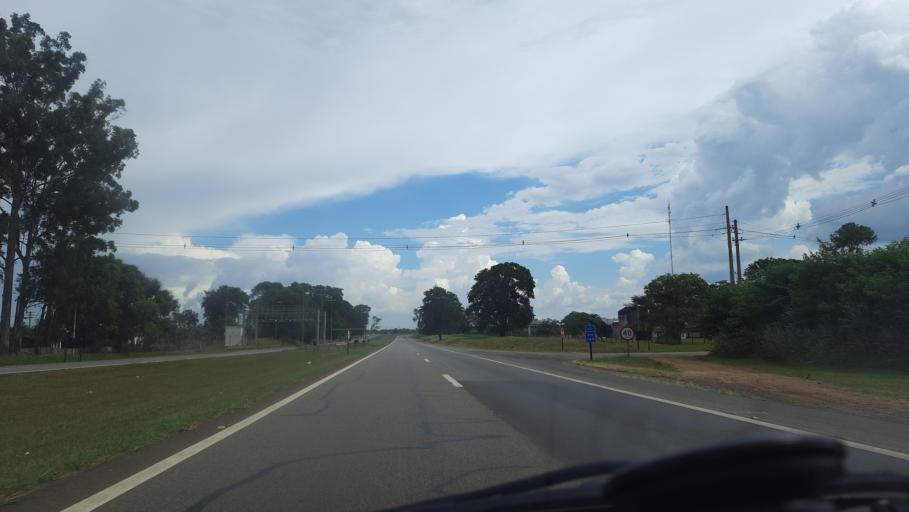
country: BR
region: Sao Paulo
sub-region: Santo Antonio De Posse
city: Santo Antonio de Posse
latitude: -22.5639
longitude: -47.0006
